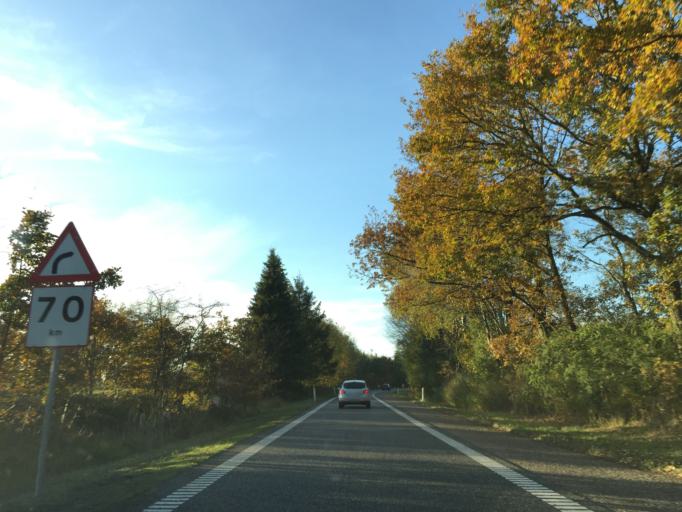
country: DK
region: South Denmark
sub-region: Aabenraa Kommune
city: Krusa
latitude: 54.8739
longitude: 9.3822
